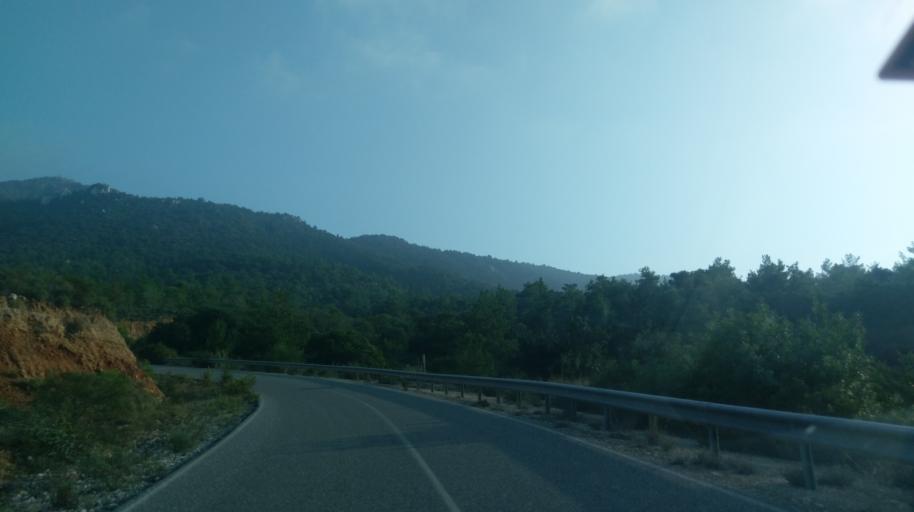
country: CY
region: Ammochostos
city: Trikomo
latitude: 35.4106
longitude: 33.9043
